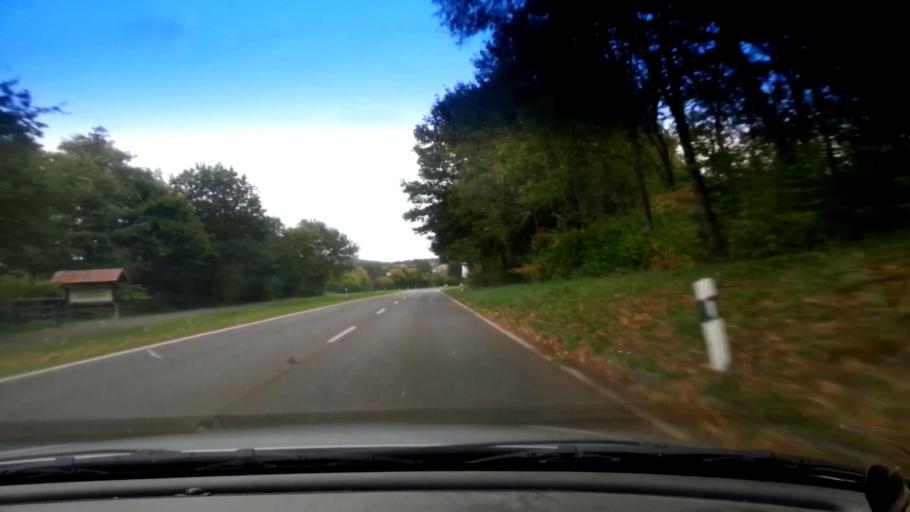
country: DE
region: Bavaria
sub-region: Upper Franconia
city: Lauter
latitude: 49.9715
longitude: 10.7891
